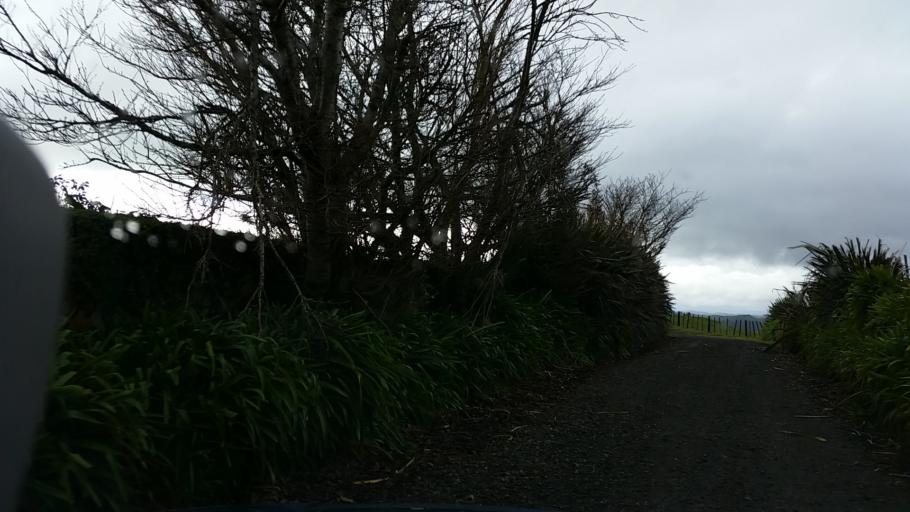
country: NZ
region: Taranaki
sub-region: South Taranaki District
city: Eltham
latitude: -39.2760
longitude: 174.3394
